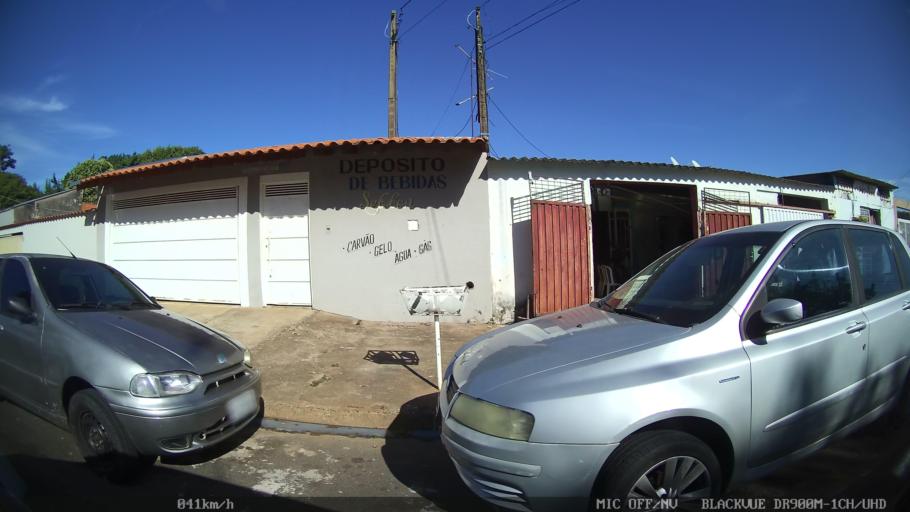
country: BR
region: Sao Paulo
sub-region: Franca
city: Franca
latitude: -20.4957
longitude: -47.4164
